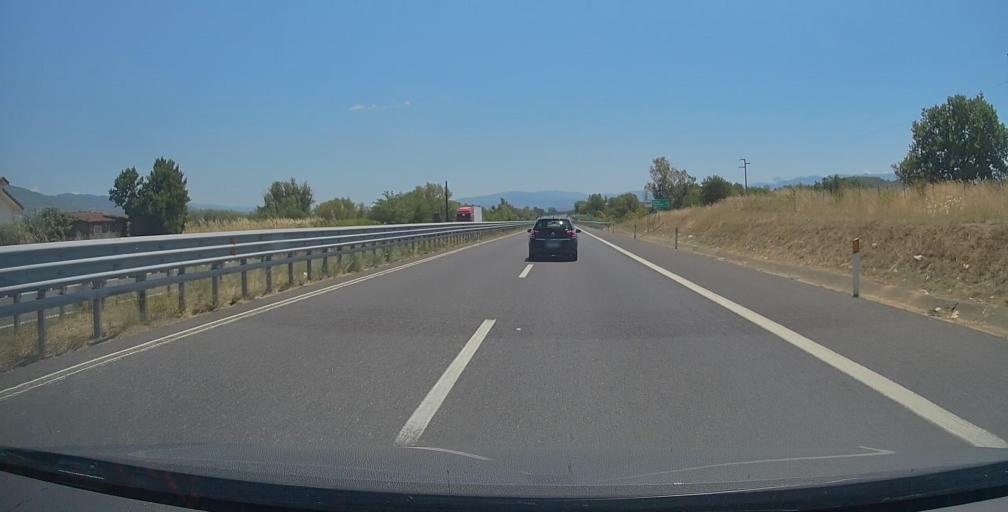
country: IT
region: Calabria
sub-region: Provincia di Cosenza
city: Stazione Montalto-Coretto
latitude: 39.4046
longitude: 16.2439
